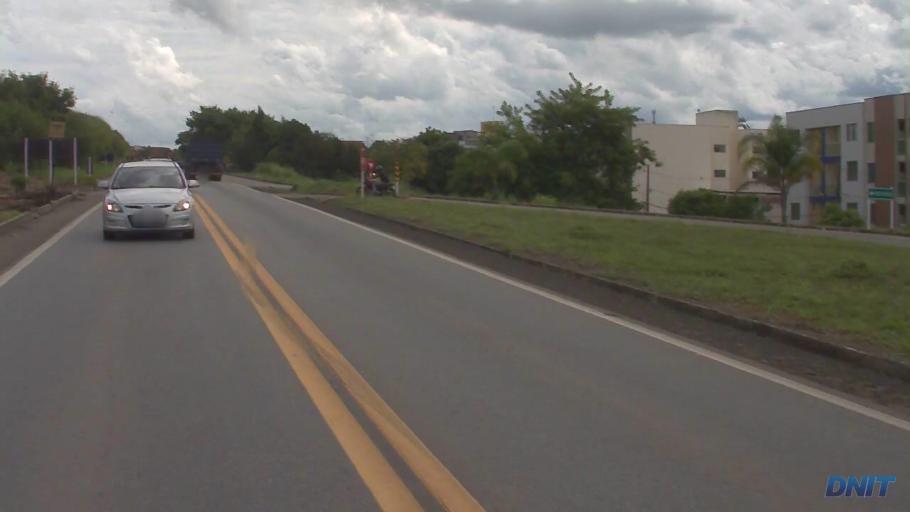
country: BR
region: Minas Gerais
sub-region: Ipatinga
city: Ipatinga
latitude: -19.4553
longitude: -42.5228
